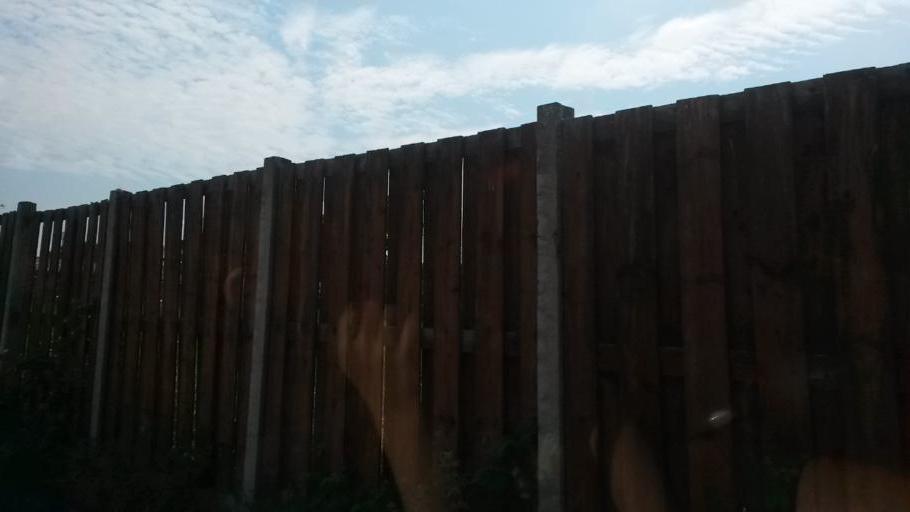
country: IE
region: Leinster
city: Donabate
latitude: 53.4862
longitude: -6.1522
